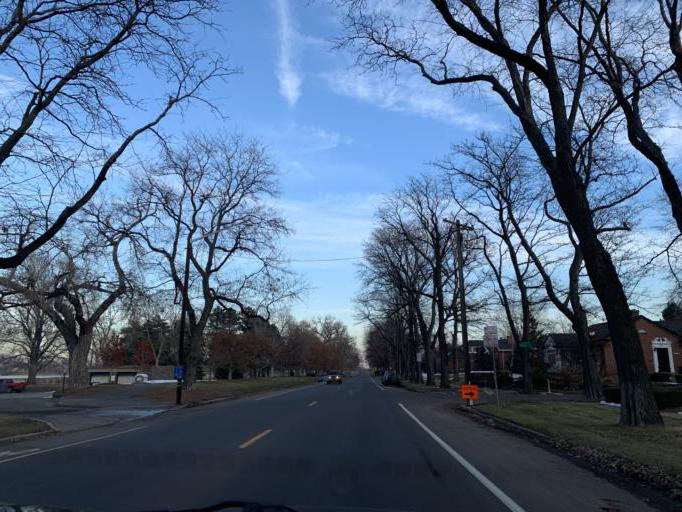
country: US
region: Colorado
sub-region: Adams County
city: Berkley
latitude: 39.7802
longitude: -105.0335
